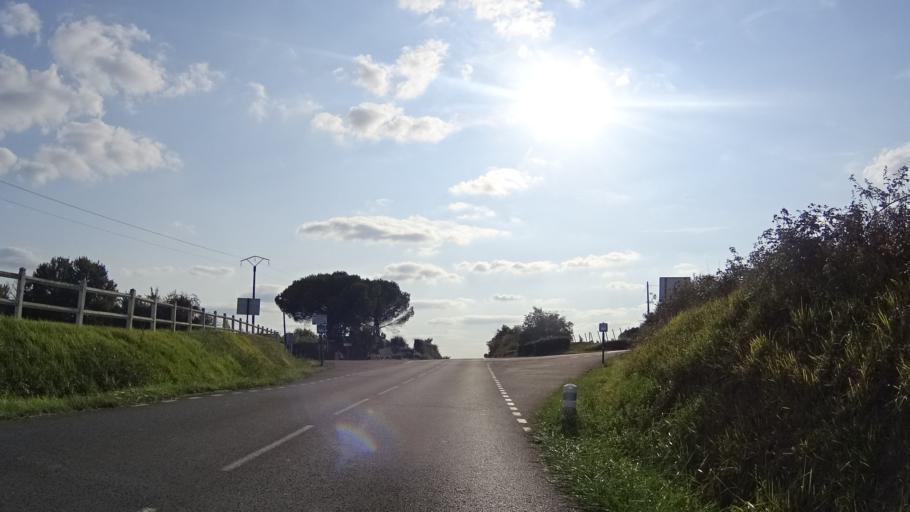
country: FR
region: Pays de la Loire
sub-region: Departement de Maine-et-Loire
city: Savennieres
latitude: 47.3942
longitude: -0.6454
